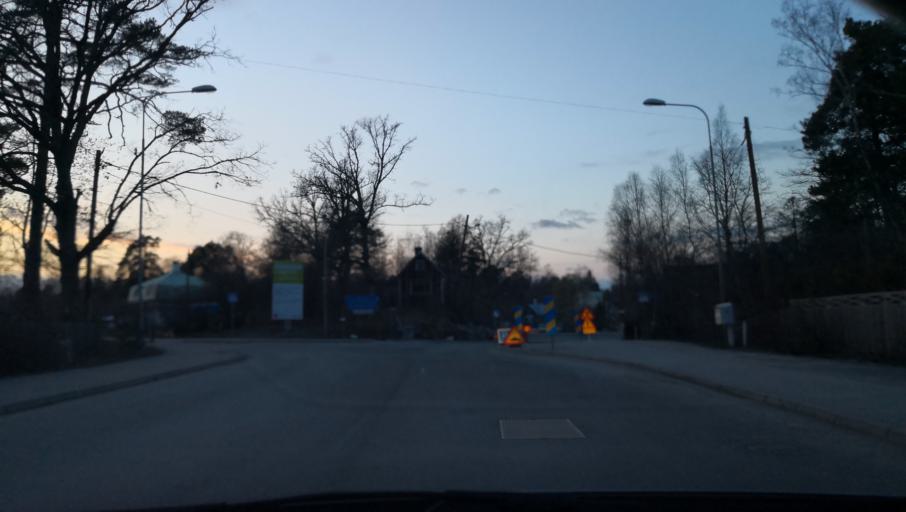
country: SE
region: Stockholm
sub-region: Nacka Kommun
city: Kummelnas
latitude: 59.3431
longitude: 18.2920
